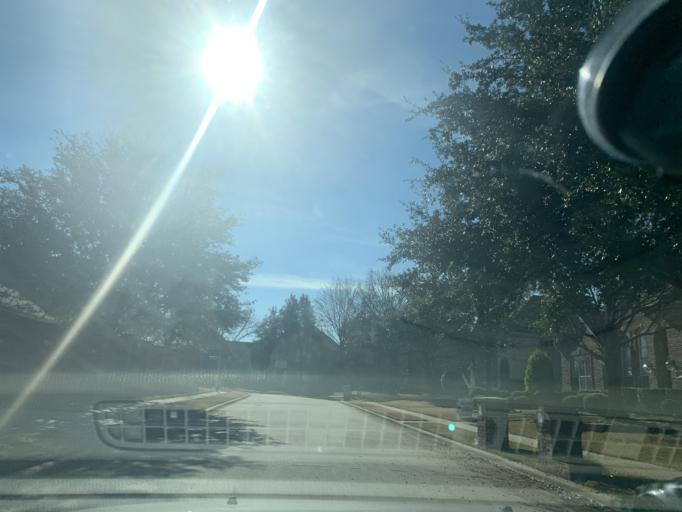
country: US
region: Texas
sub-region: Denton County
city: The Colony
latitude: 33.0527
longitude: -96.8160
